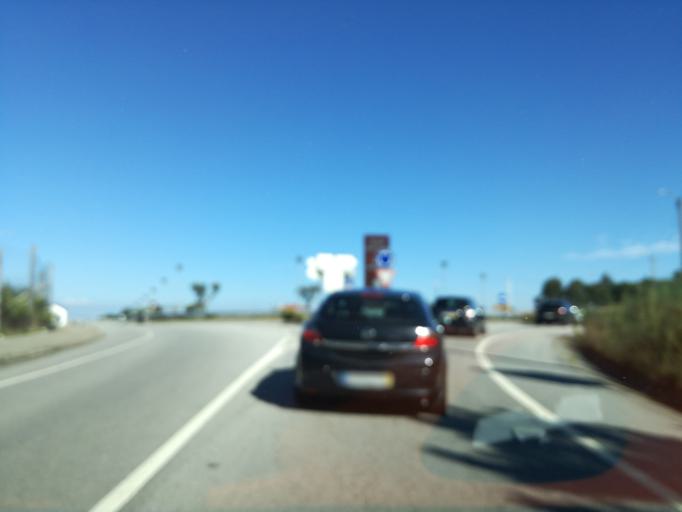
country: PT
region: Porto
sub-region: Pacos de Ferreira
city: Seroa
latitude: 41.2576
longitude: -8.4441
